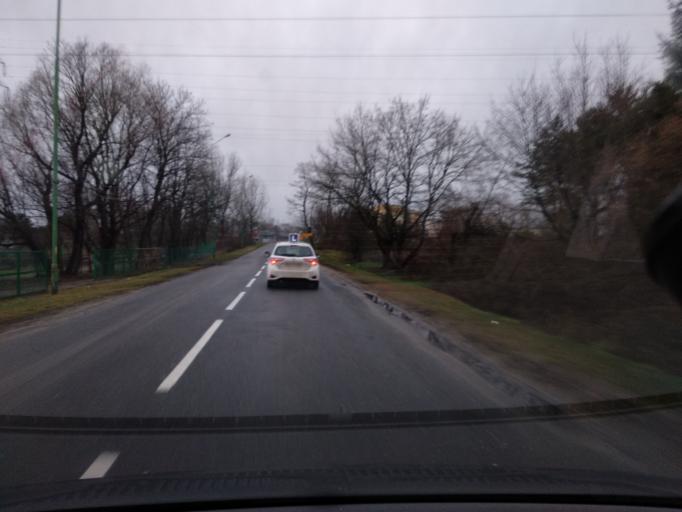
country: PL
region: Lower Silesian Voivodeship
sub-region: Powiat polkowicki
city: Polkowice
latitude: 51.4962
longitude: 16.0716
